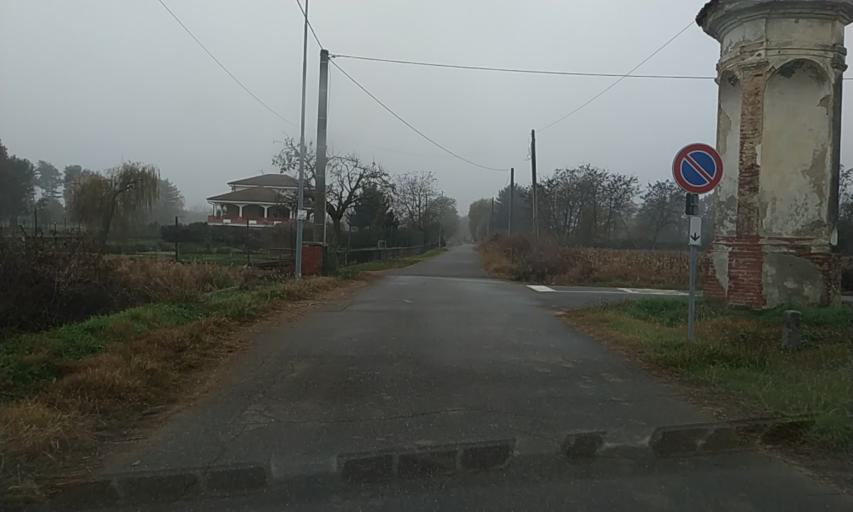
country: IT
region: Piedmont
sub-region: Provincia di Vercelli
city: Alice Castello
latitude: 45.3655
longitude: 8.0660
